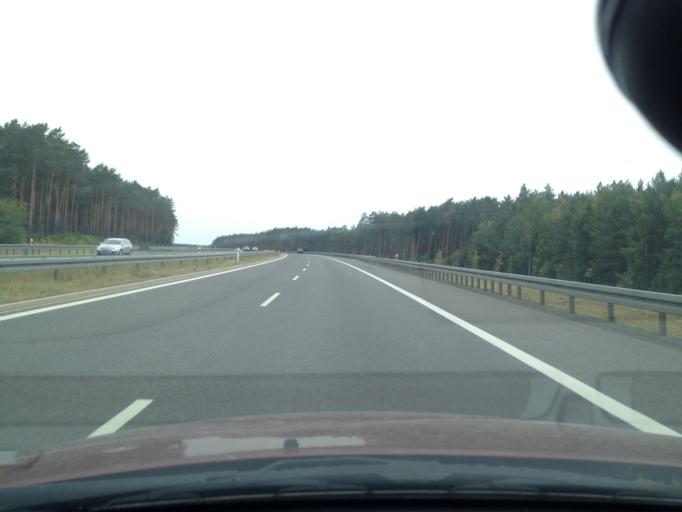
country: PL
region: Lubusz
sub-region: Powiat gorzowski
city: Deszczno
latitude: 52.6383
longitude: 15.3673
